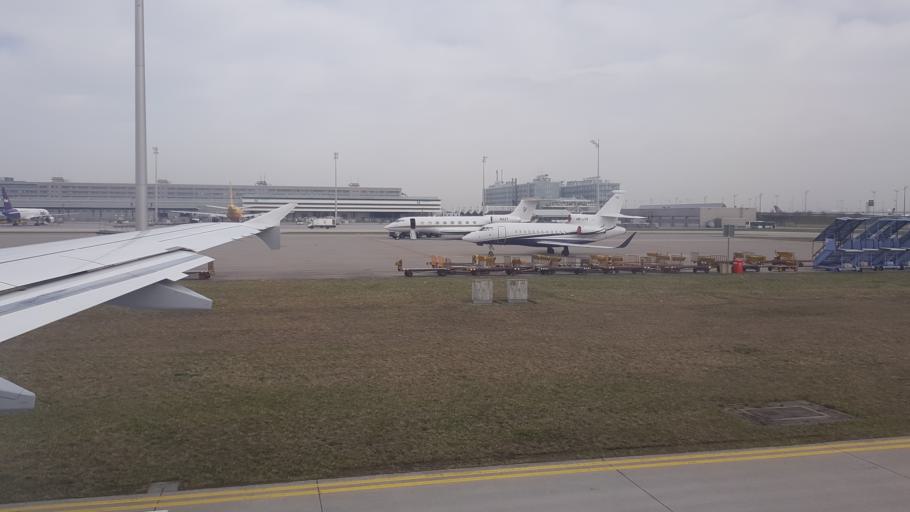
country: DE
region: Bavaria
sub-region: Upper Bavaria
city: Hallbergmoos
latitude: 48.3460
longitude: 11.7726
